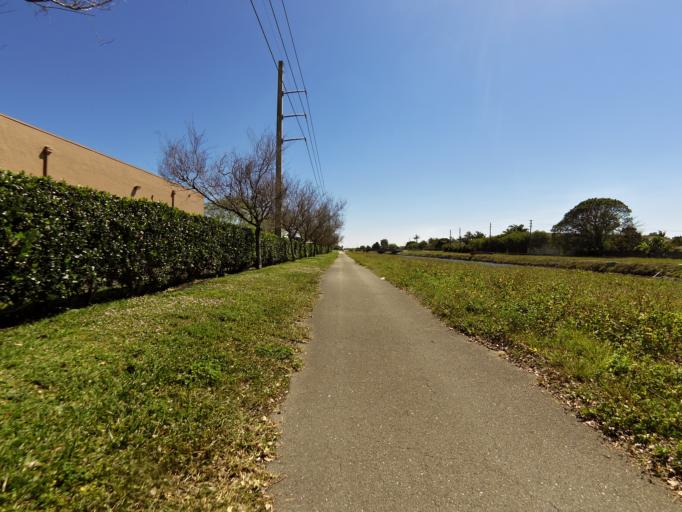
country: US
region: Florida
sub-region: Broward County
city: Tamarac
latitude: 26.1703
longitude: -80.2978
